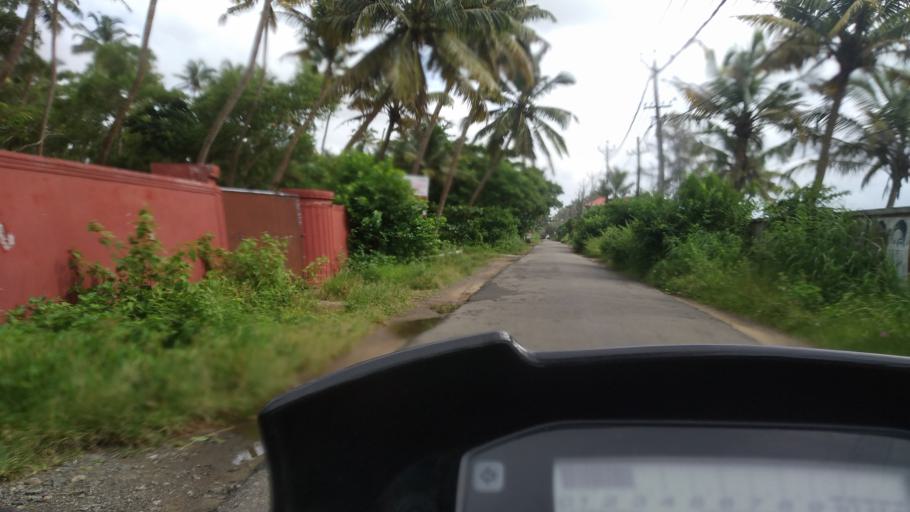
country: IN
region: Kerala
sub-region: Thrissur District
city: Kodungallur
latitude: 10.1467
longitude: 76.1769
